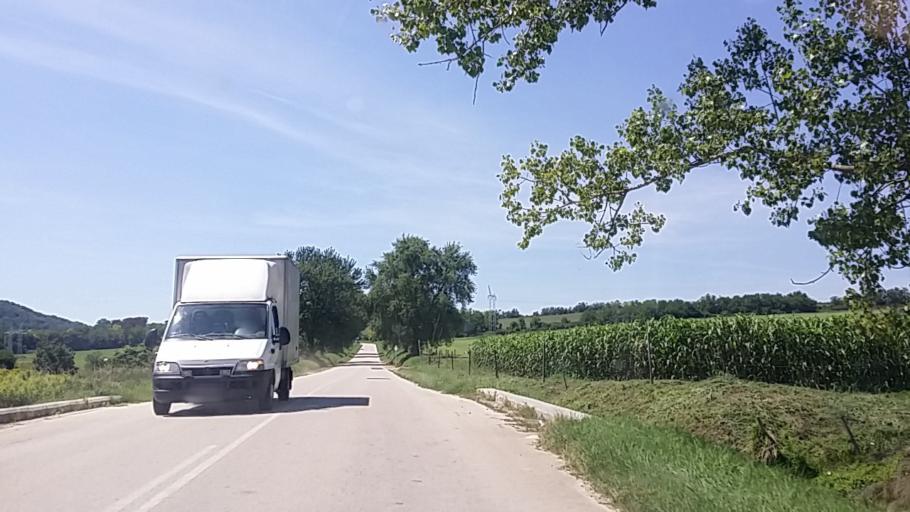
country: HU
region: Somogy
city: Tab
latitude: 46.7393
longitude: 18.0678
